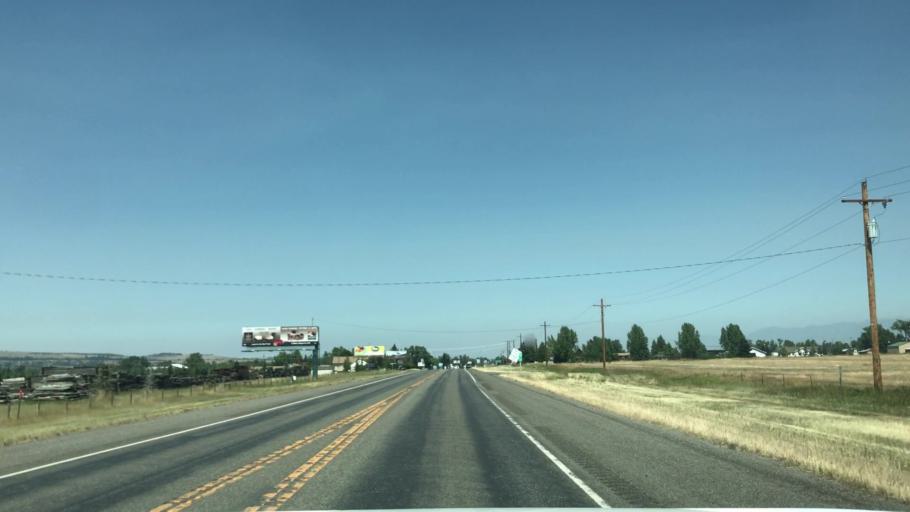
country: US
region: Montana
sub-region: Gallatin County
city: Four Corners
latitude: 45.5866
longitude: -111.1970
